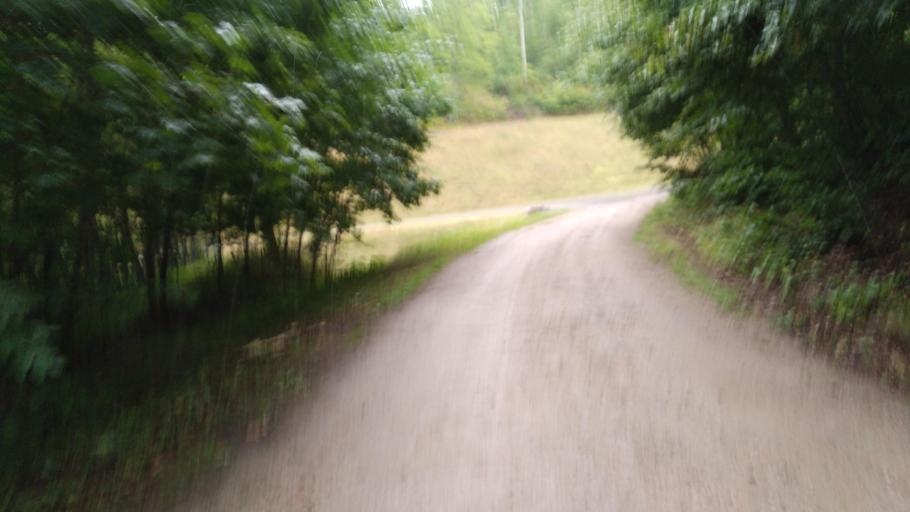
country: PL
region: Pomeranian Voivodeship
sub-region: Powiat wejherowski
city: Goscicino
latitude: 54.6329
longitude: 18.1338
